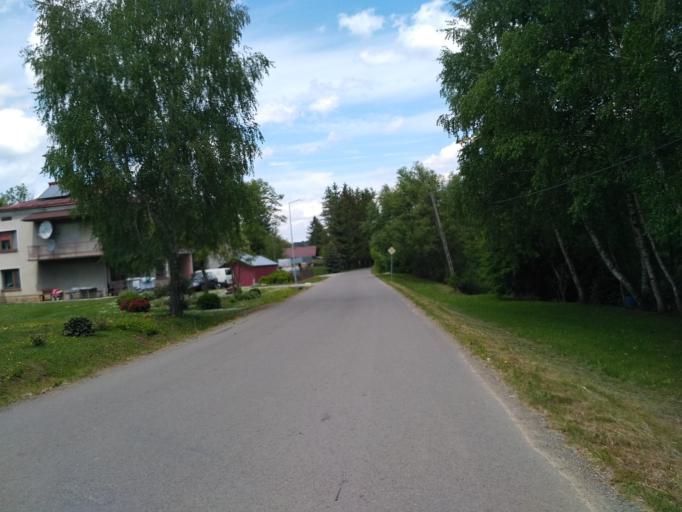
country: PL
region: Subcarpathian Voivodeship
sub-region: Powiat krosnienski
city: Dukla
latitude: 49.5931
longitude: 21.6221
